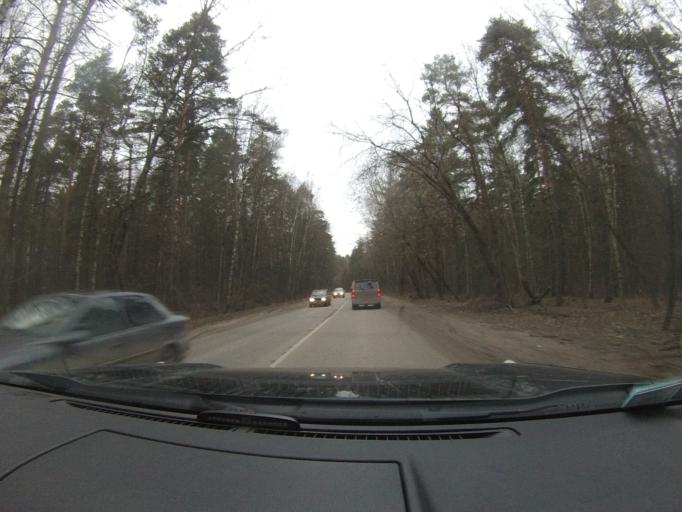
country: RU
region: Moskovskaya
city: Voskresensk
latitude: 55.3354
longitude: 38.6752
